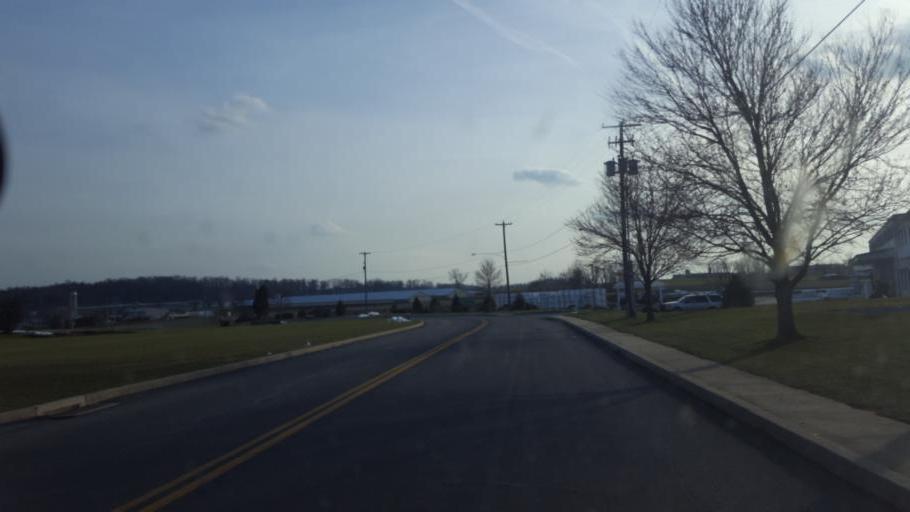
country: US
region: Pennsylvania
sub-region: Lancaster County
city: New Holland
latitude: 40.0890
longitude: -76.0880
